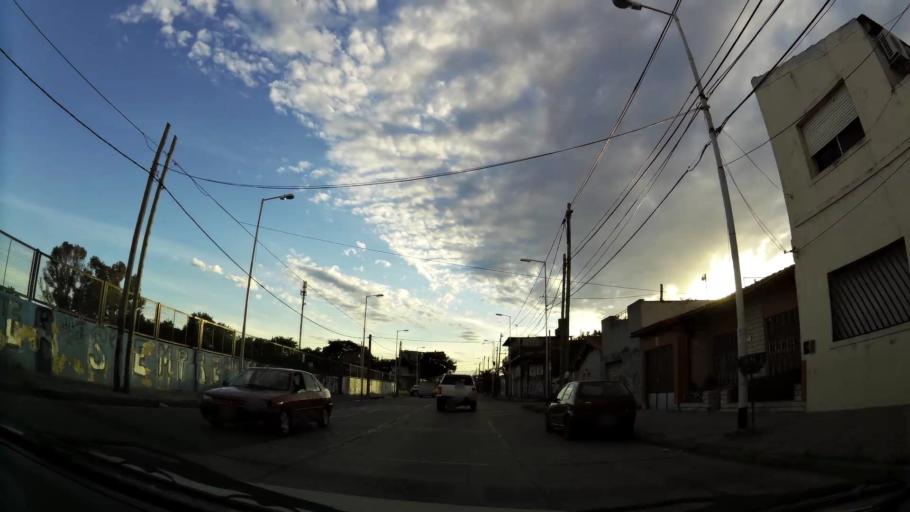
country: AR
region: Buenos Aires
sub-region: Partido de Avellaneda
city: Avellaneda
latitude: -34.7037
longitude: -58.3414
